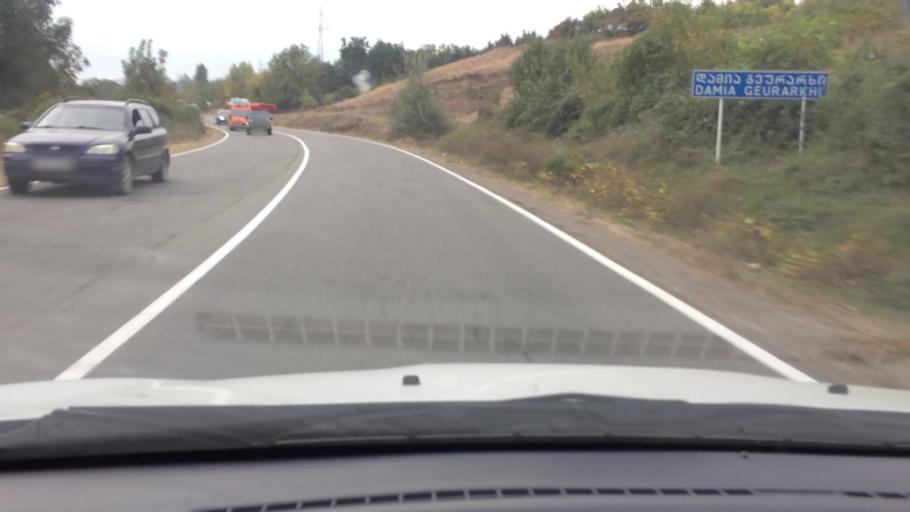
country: GE
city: Naghvarevi
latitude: 41.3045
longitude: 44.7899
